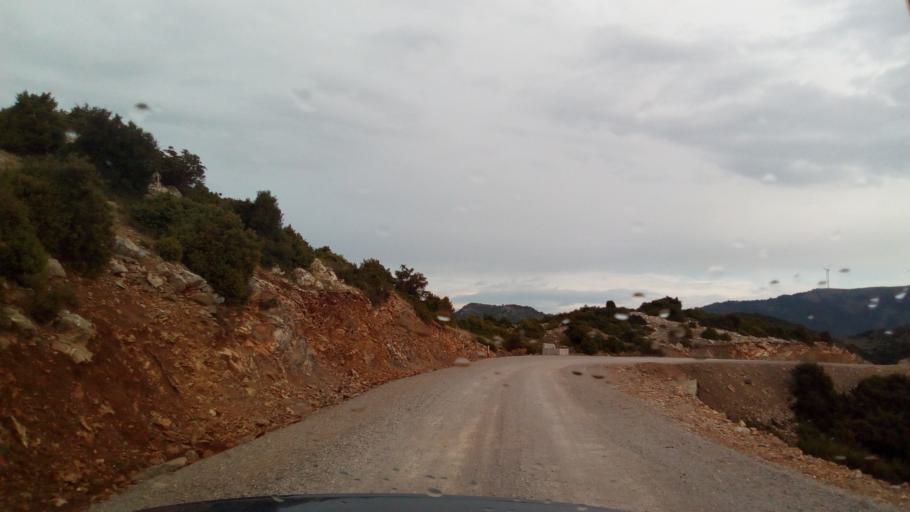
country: GR
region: West Greece
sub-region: Nomos Achaias
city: Kamarai
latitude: 38.4301
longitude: 22.0500
